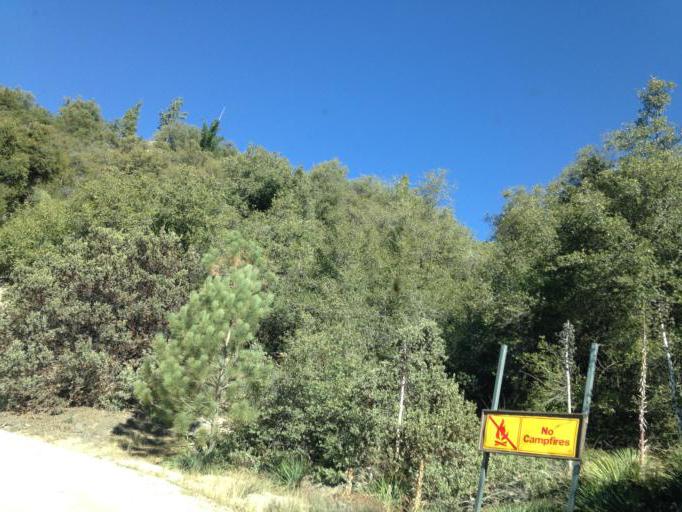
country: US
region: California
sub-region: Riverside County
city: Idyllwild-Pine Cove
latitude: 33.7974
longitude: -116.7562
